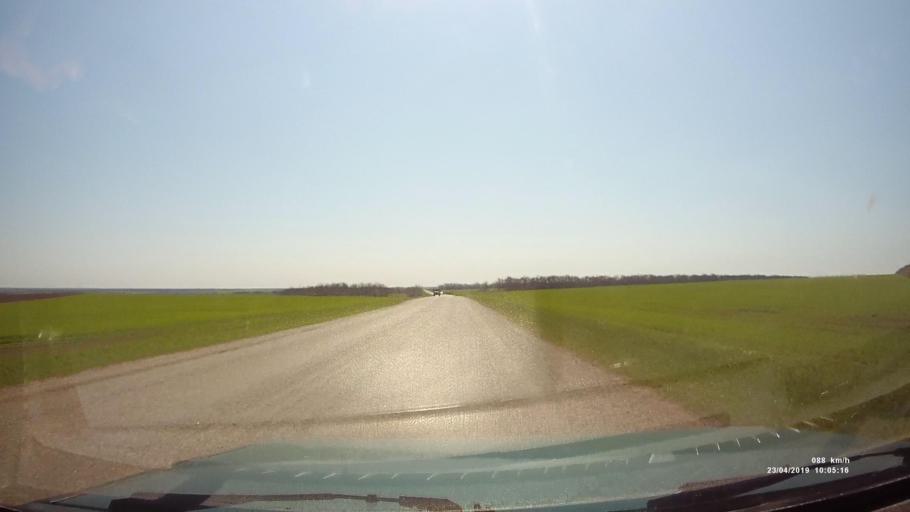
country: RU
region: Rostov
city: Sovetskoye
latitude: 46.7424
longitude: 42.2170
